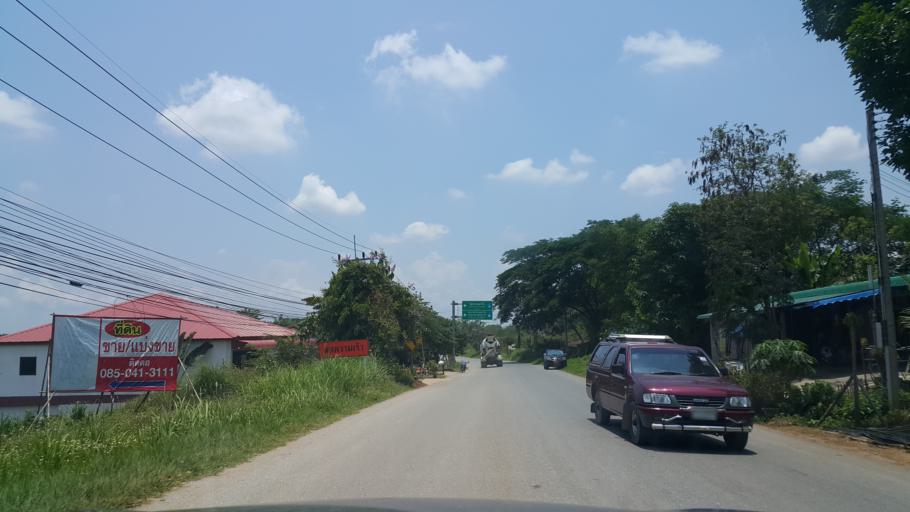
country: TH
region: Chiang Rai
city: Chiang Rai
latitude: 19.9423
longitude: 99.8046
